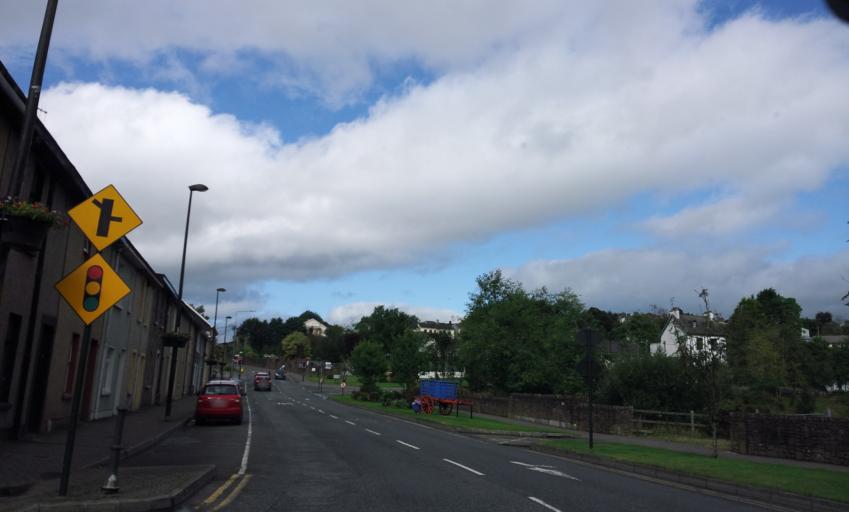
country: IE
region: Munster
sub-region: County Cork
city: Blarney
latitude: 51.9339
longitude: -8.5616
